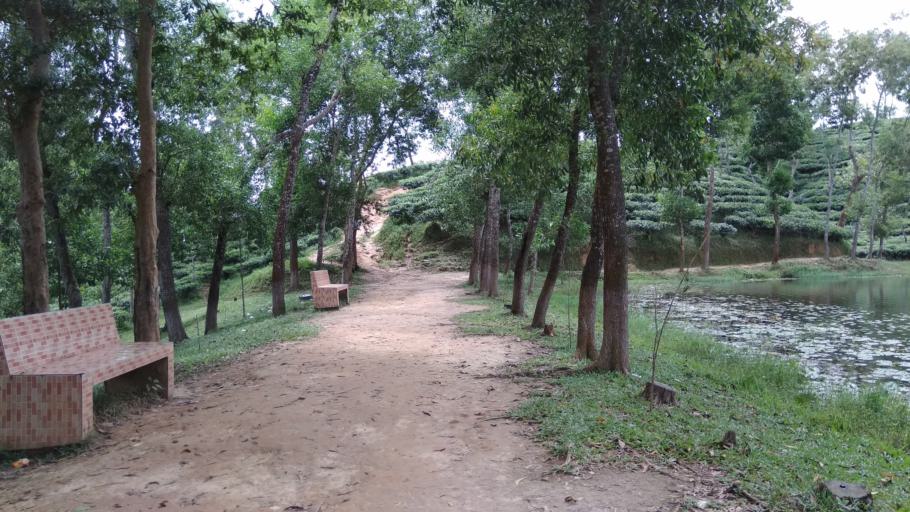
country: IN
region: Tripura
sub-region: Dhalai
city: Kamalpur
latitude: 24.2820
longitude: 91.8215
